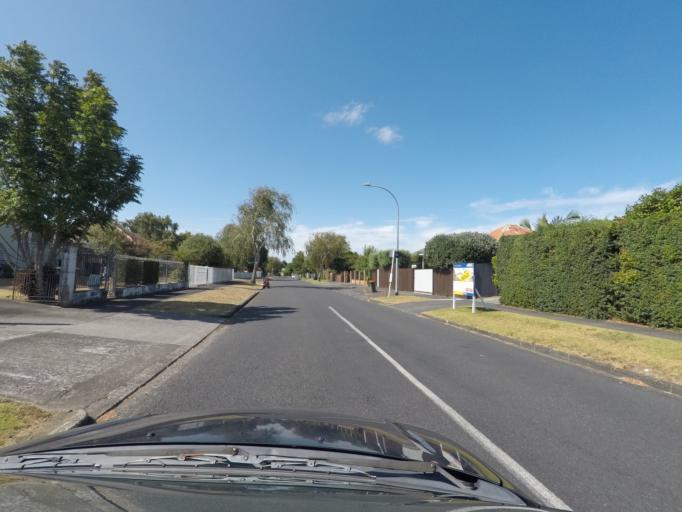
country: NZ
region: Auckland
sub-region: Auckland
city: Rosebank
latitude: -36.8874
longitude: 174.6777
